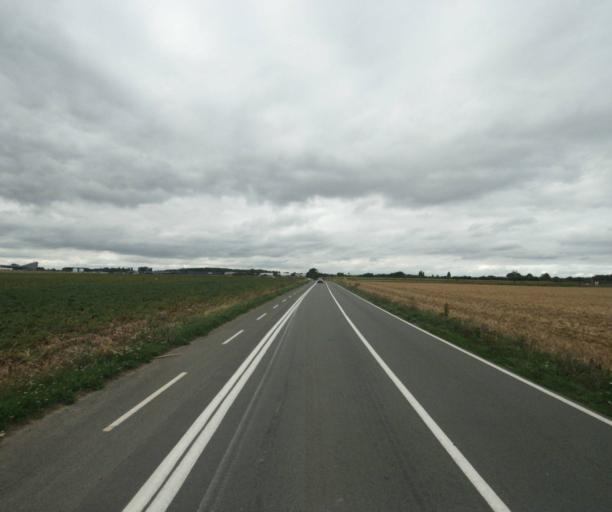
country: FR
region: Nord-Pas-de-Calais
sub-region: Departement du Nord
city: Fretin
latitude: 50.5660
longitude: 3.1258
